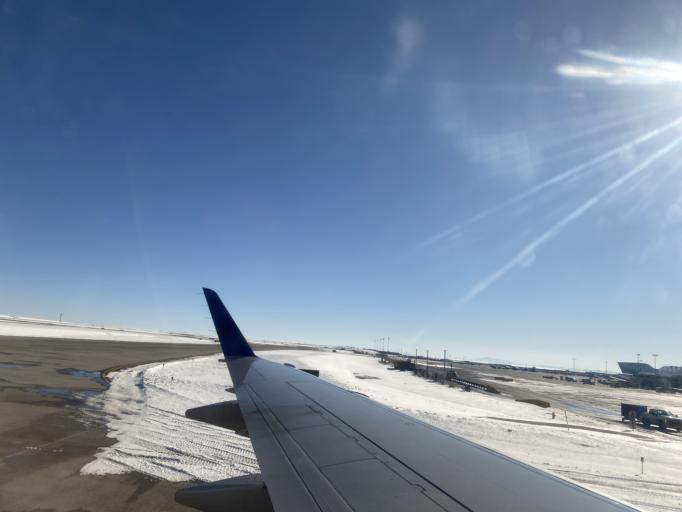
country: US
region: Colorado
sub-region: Weld County
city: Lochbuie
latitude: 39.8601
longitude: -104.6637
